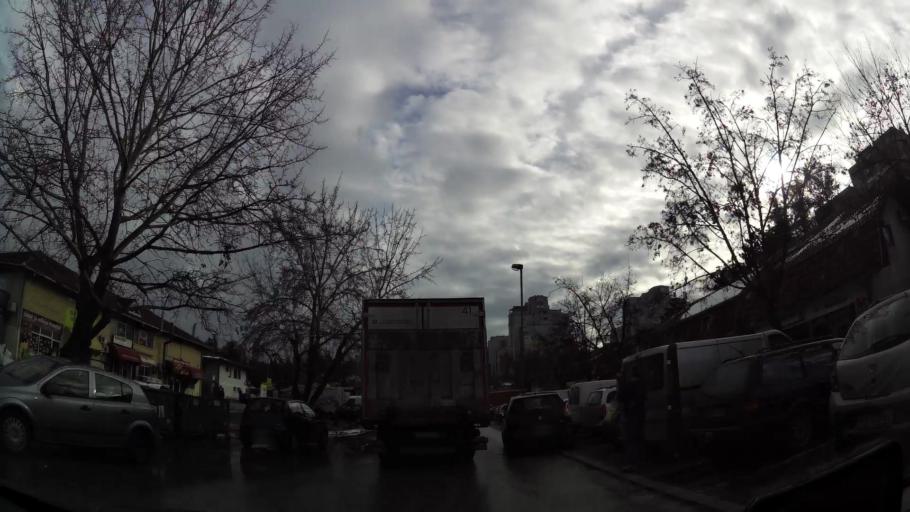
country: RS
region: Central Serbia
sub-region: Belgrade
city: Rakovica
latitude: 44.7420
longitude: 20.4185
